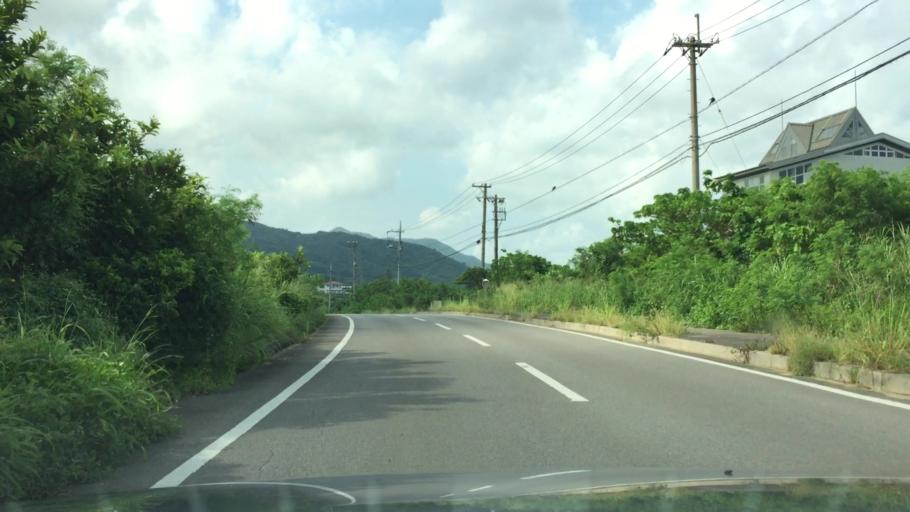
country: JP
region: Okinawa
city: Ishigaki
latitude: 24.3945
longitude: 124.1955
